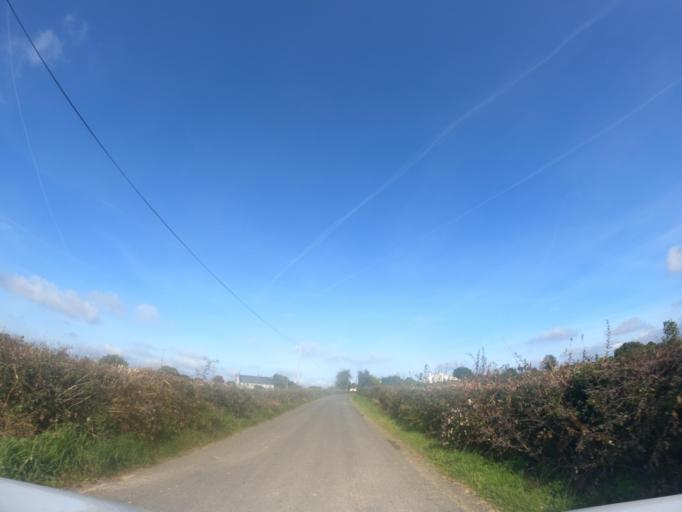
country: FR
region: Poitou-Charentes
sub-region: Departement des Deux-Sevres
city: Courlay
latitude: 46.7886
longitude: -0.5653
